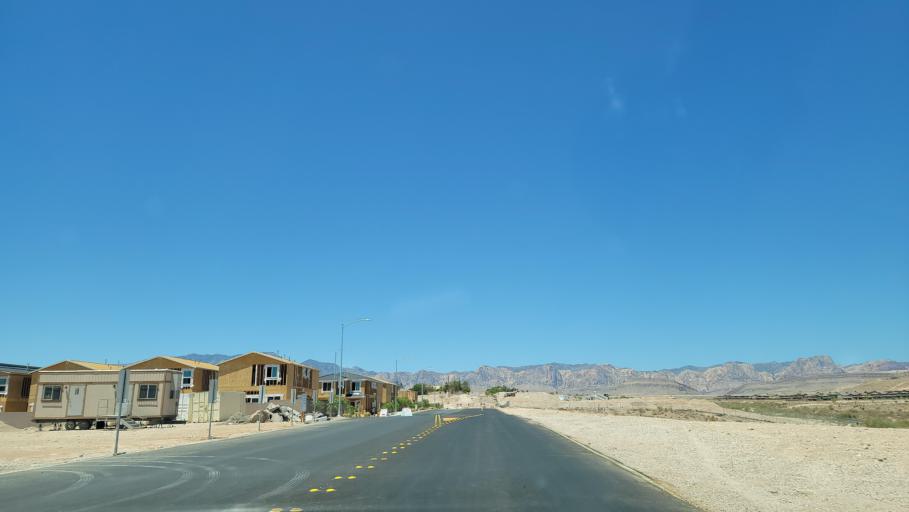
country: US
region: Nevada
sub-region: Clark County
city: Enterprise
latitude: 36.0264
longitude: -115.3004
